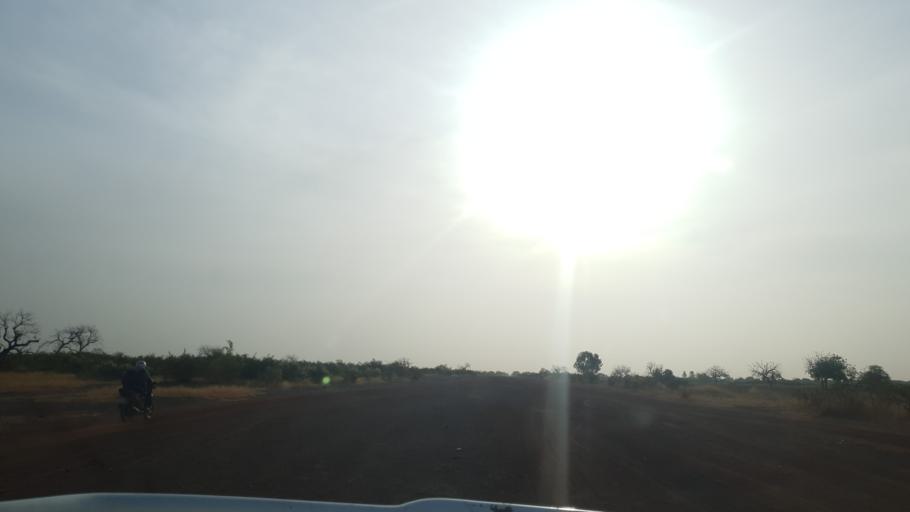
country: ML
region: Koulikoro
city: Dioila
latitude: 12.7667
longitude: -6.9199
